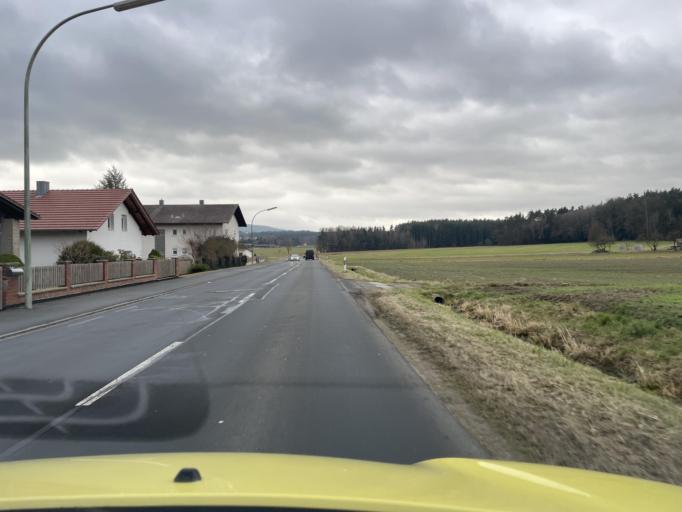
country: DE
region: Bavaria
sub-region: Upper Palatinate
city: Cham
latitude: 49.1888
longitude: 12.6704
